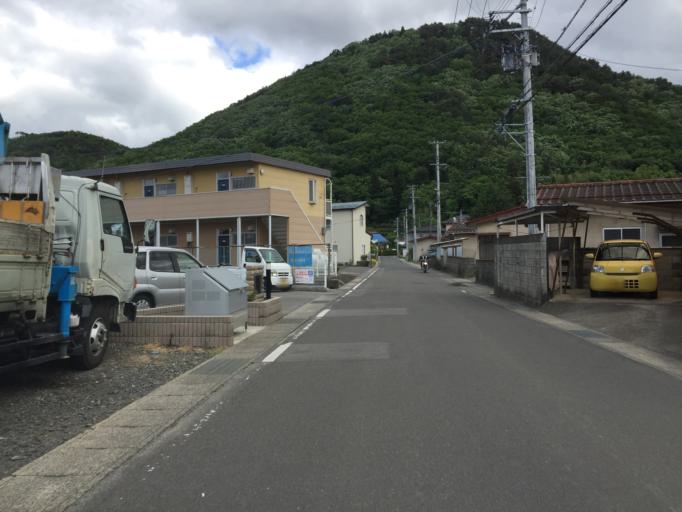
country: JP
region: Fukushima
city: Fukushima-shi
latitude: 37.7756
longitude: 140.4593
